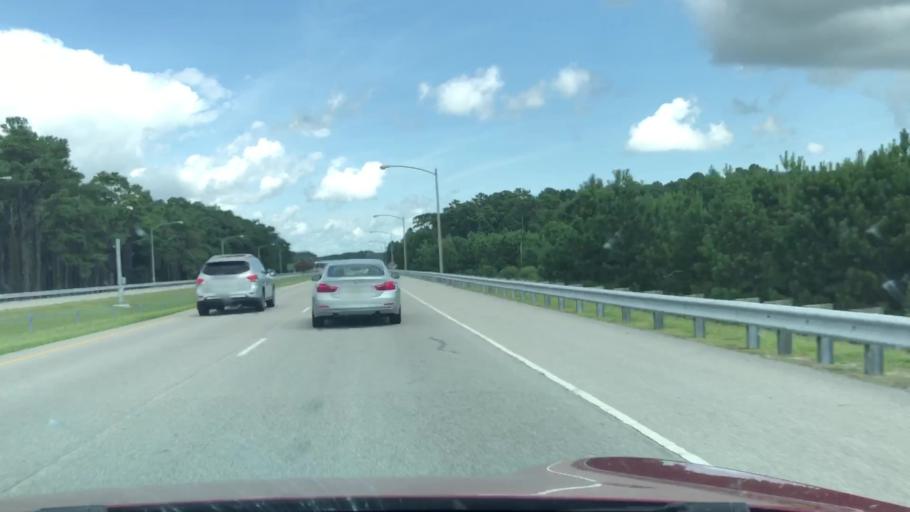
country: US
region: Virginia
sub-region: Northampton County
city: Cape Charles
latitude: 37.1251
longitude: -75.9680
